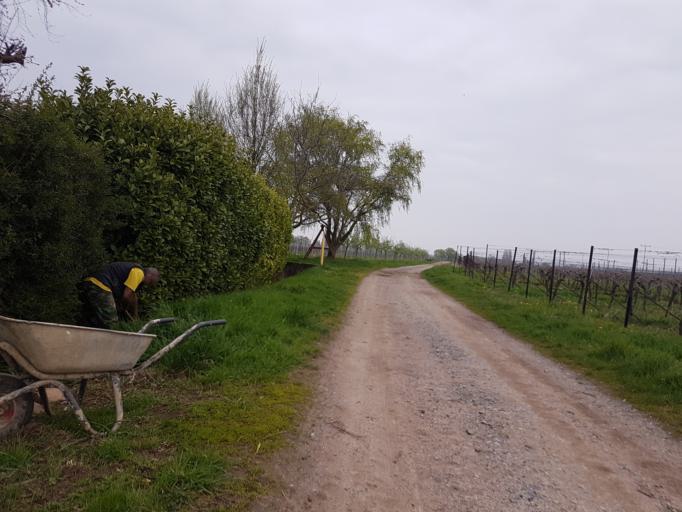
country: DE
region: Rheinland-Pfalz
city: Flemlingen
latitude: 49.2434
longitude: 8.0996
